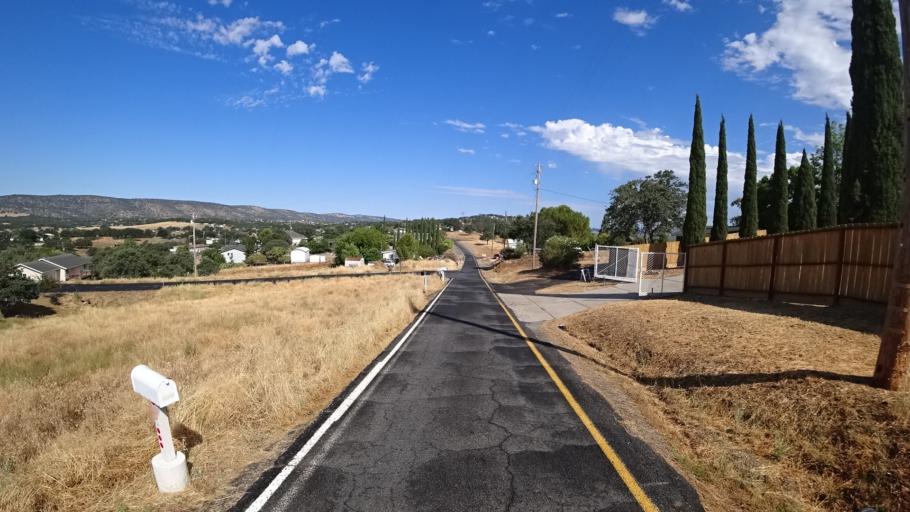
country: US
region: California
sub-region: Calaveras County
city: Copperopolis
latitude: 37.9144
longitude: -120.6160
